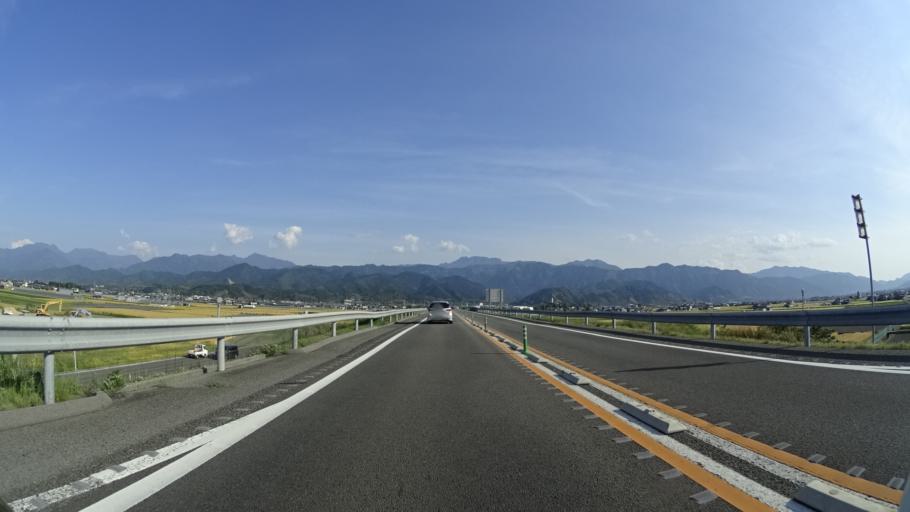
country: JP
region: Ehime
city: Saijo
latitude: 33.9074
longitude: 133.0742
